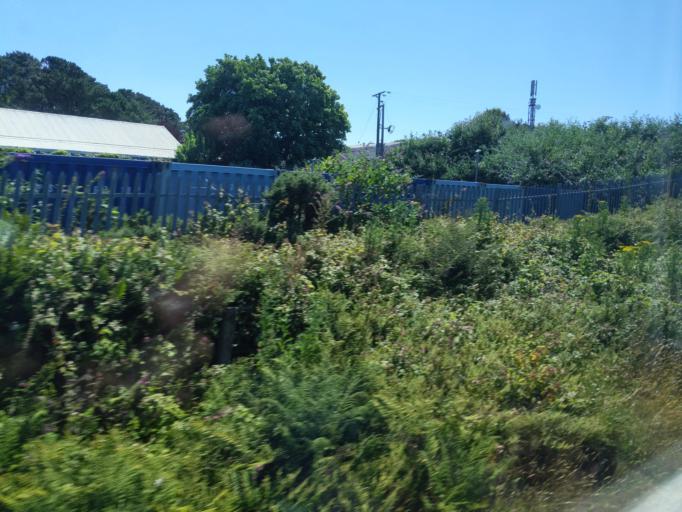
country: GB
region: England
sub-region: Cornwall
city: St. Day
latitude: 50.2507
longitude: -5.2065
